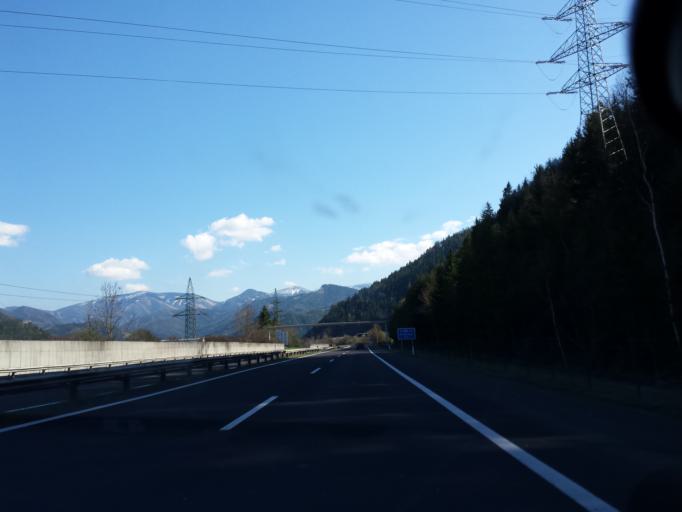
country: AT
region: Styria
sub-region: Politischer Bezirk Leoben
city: Traboch
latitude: 47.3607
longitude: 14.9996
